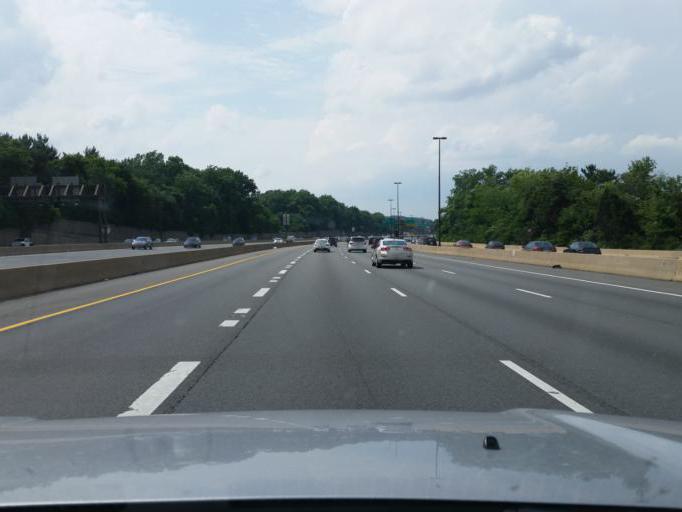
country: US
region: Maryland
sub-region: Montgomery County
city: Rockville
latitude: 39.0749
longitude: -77.1657
